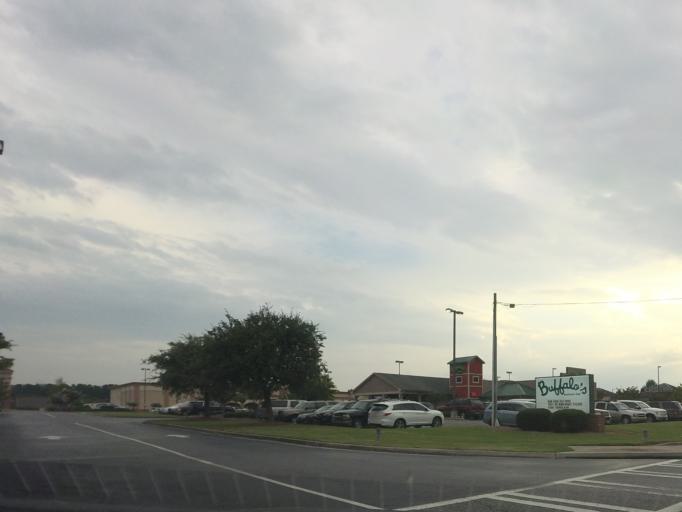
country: US
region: Georgia
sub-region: Bibb County
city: West Point
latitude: 32.8798
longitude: -83.7615
